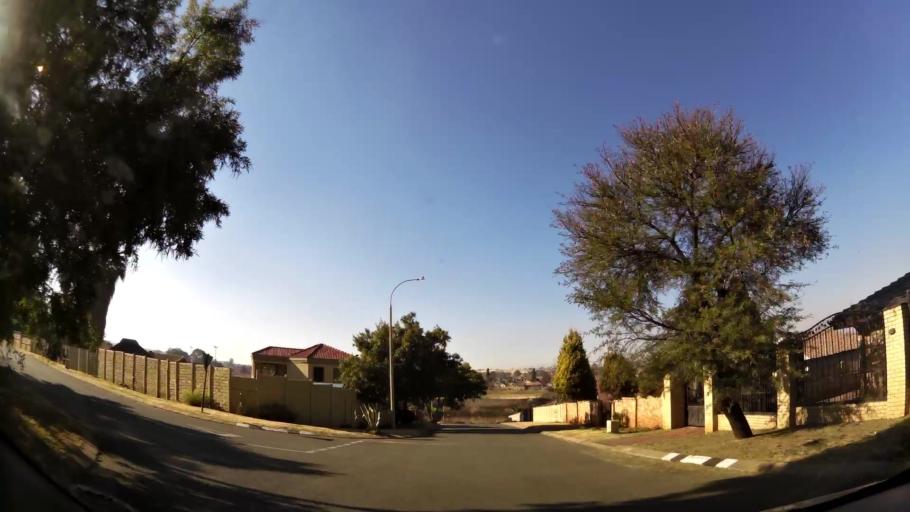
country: ZA
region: Gauteng
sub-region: City of Johannesburg Metropolitan Municipality
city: Roodepoort
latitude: -26.1529
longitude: 27.8435
